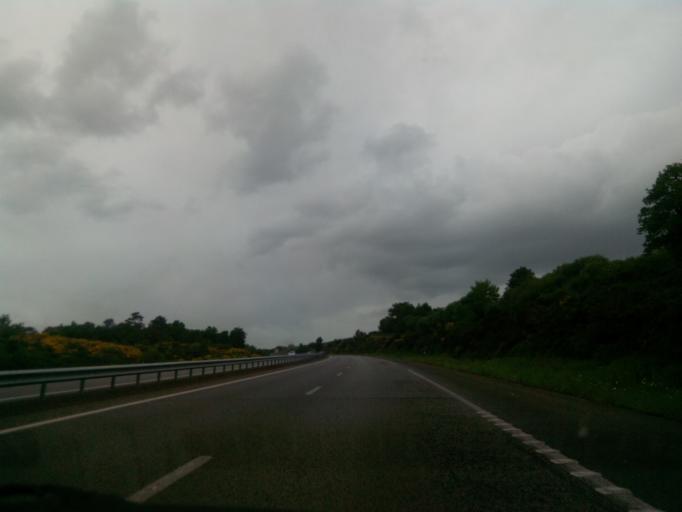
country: FR
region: Brittany
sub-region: Departement d'Ille-et-Vilaine
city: Plelan-le-Grand
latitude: 47.9571
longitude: -2.0916
